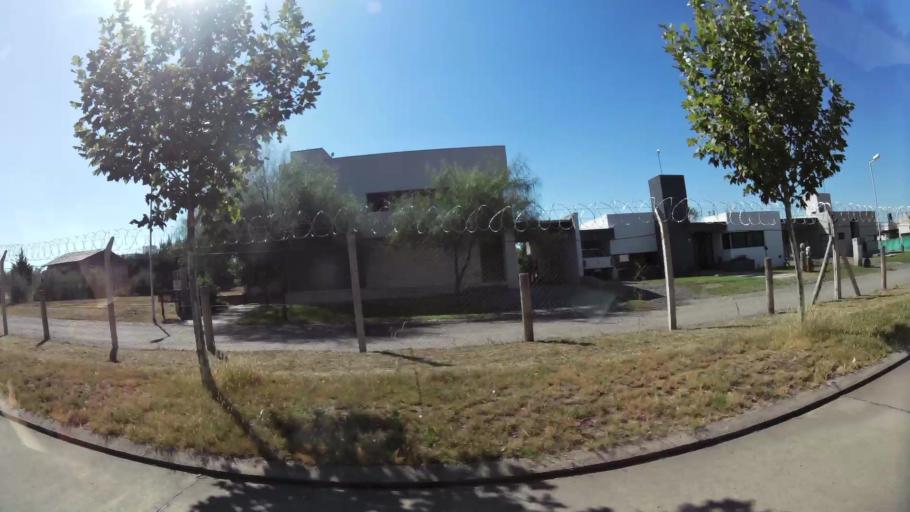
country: AR
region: Cordoba
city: Villa Allende
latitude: -31.3038
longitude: -64.2645
